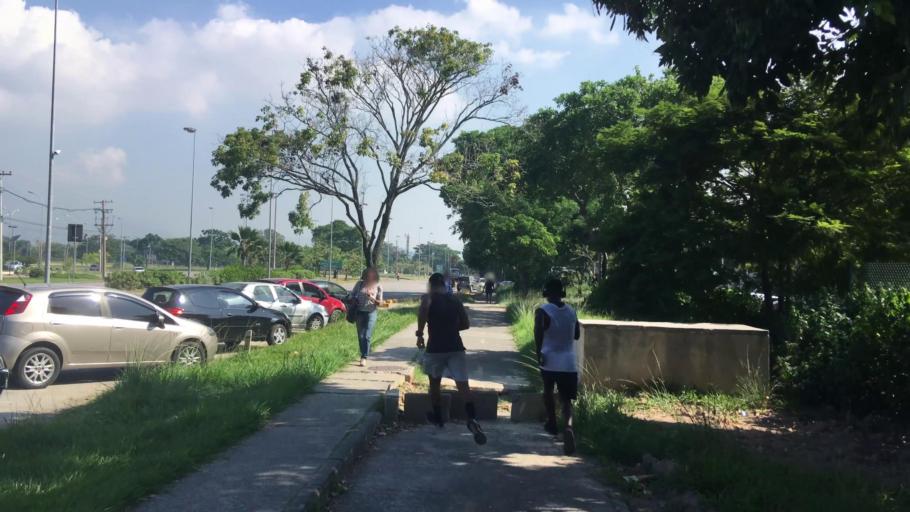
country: BR
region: Rio de Janeiro
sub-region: Rio De Janeiro
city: Rio de Janeiro
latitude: -22.8430
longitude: -43.2331
